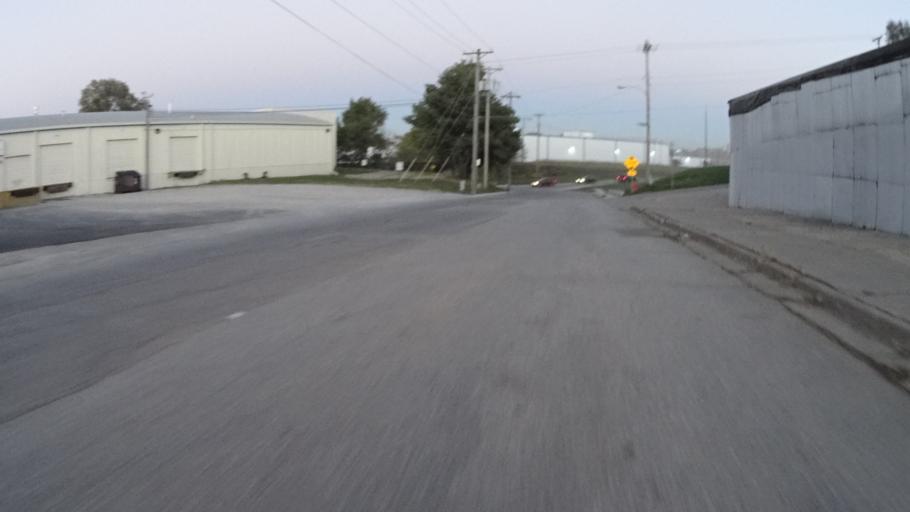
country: US
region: Nebraska
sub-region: Douglas County
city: Omaha
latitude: 41.2173
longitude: -95.9625
